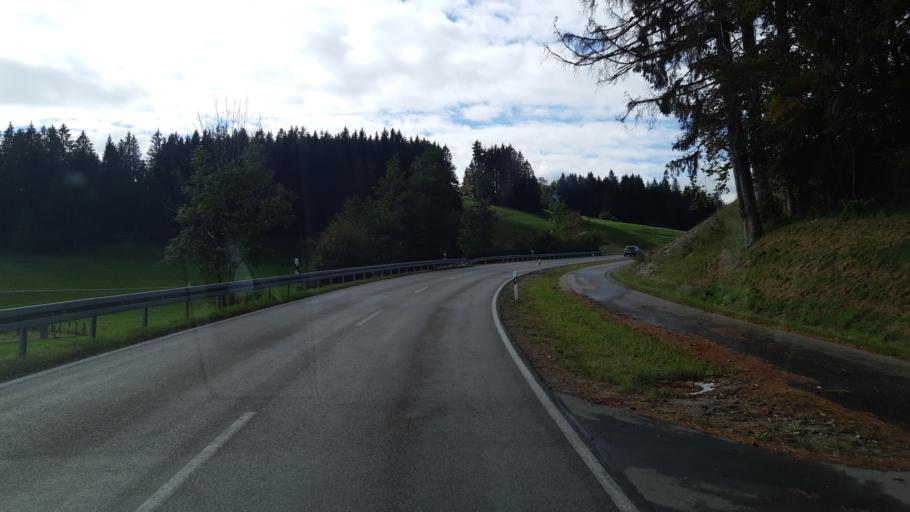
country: DE
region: Bavaria
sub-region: Swabia
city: Eisenberg
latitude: 47.6044
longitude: 10.5930
